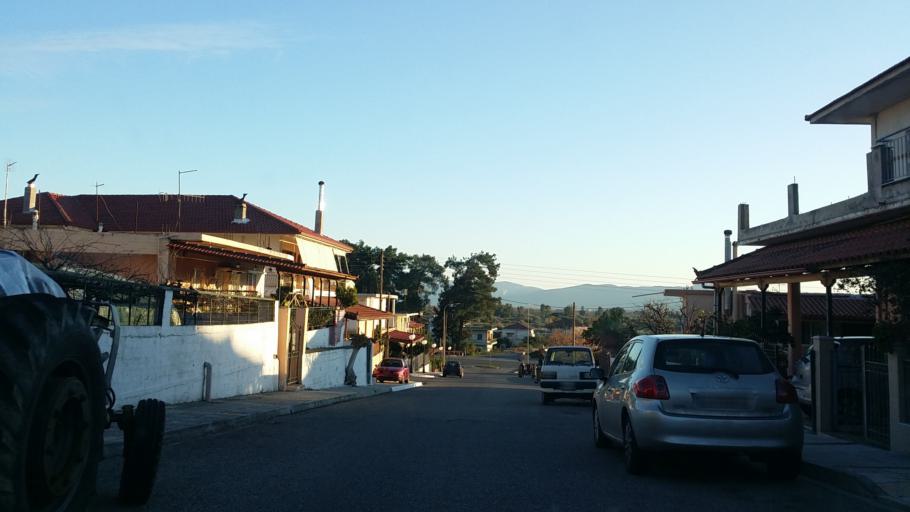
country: GR
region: West Greece
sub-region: Nomos Aitolias kai Akarnanias
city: Neapolis
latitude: 38.6682
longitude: 21.3184
